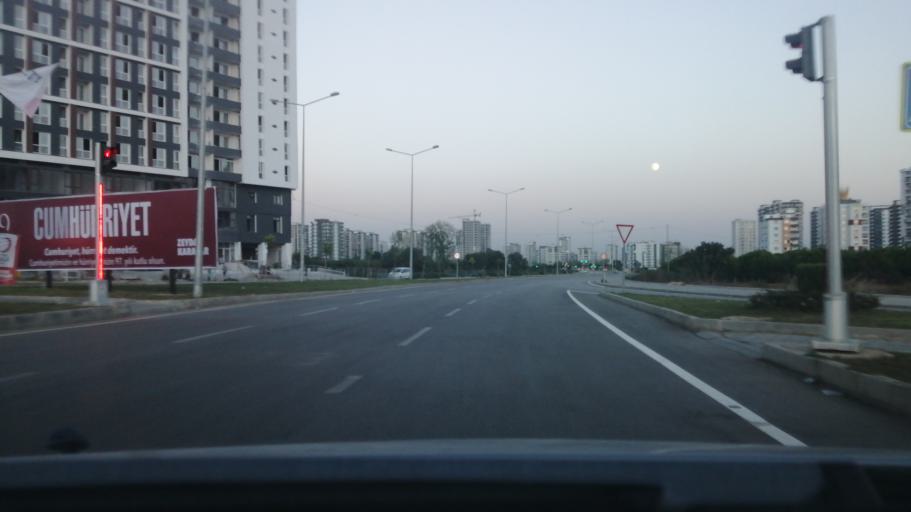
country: TR
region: Adana
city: Seyhan
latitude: 37.0153
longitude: 35.2512
